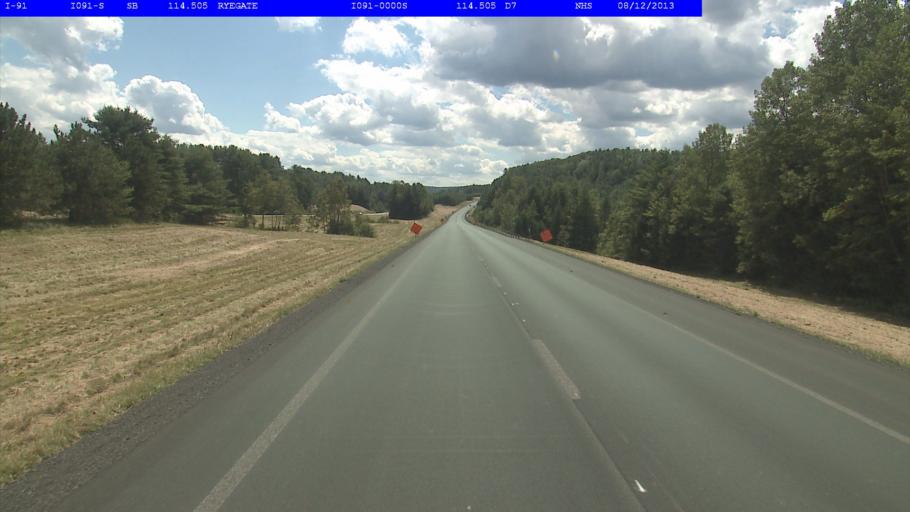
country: US
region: New Hampshire
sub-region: Grafton County
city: Woodsville
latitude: 44.2180
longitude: -72.0677
